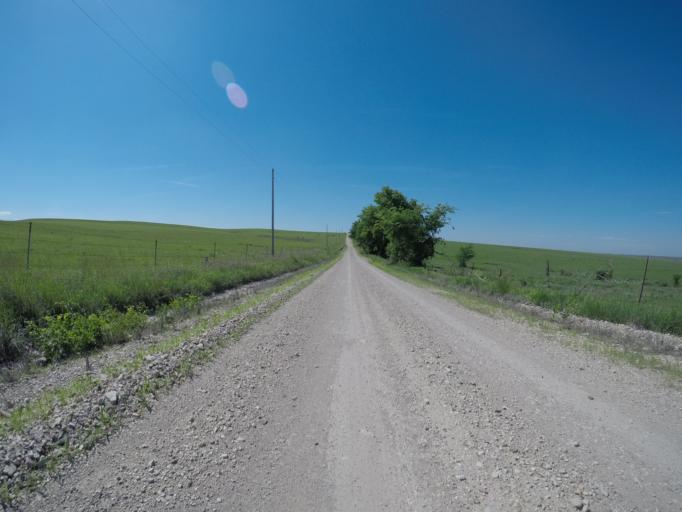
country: US
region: Kansas
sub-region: Wabaunsee County
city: Alma
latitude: 39.0059
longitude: -96.1783
